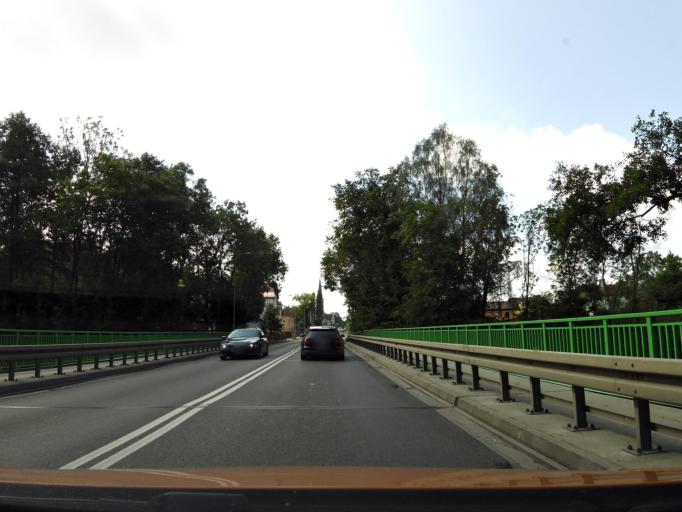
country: PL
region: West Pomeranian Voivodeship
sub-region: Powiat gryficki
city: Ploty
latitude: 53.8074
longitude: 15.2726
